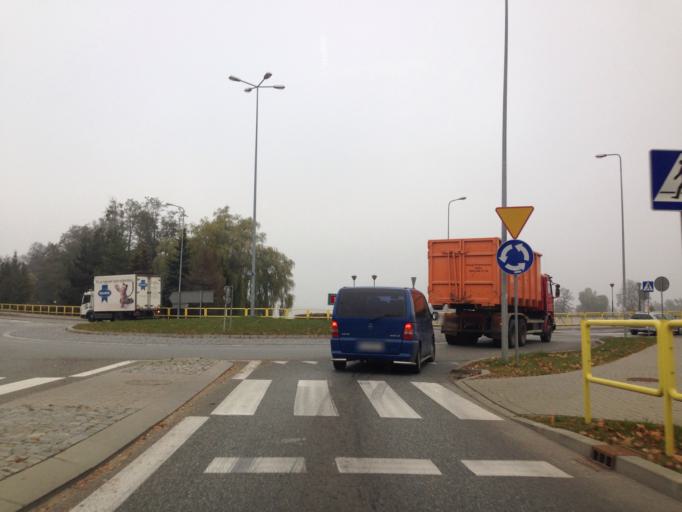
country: PL
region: Warmian-Masurian Voivodeship
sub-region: Powiat ilawski
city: Ilawa
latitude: 53.5970
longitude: 19.5541
